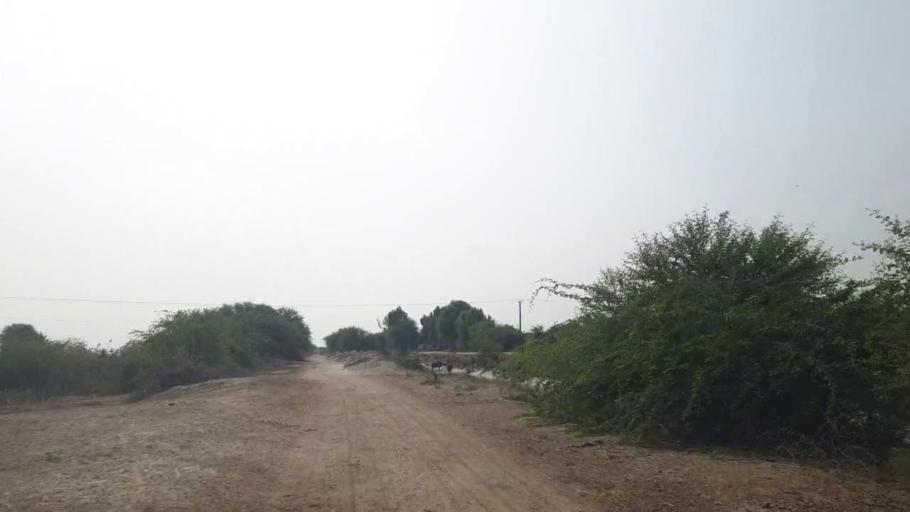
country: PK
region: Sindh
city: Badin
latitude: 24.6072
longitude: 68.7204
